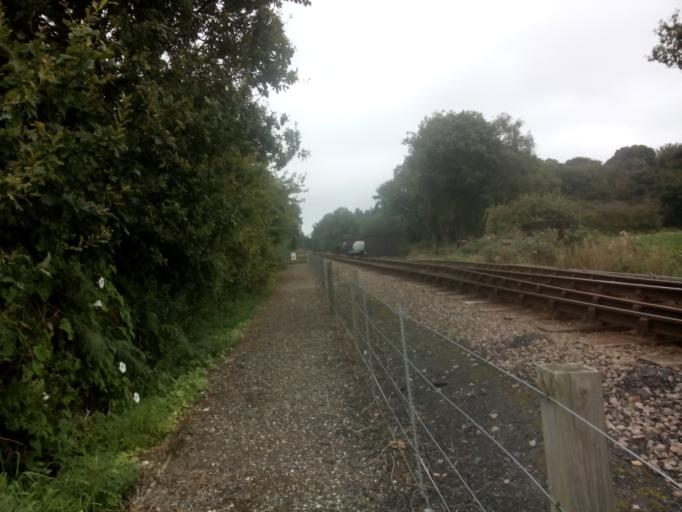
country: GB
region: England
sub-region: Norfolk
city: Briston
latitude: 52.9189
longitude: 1.1139
